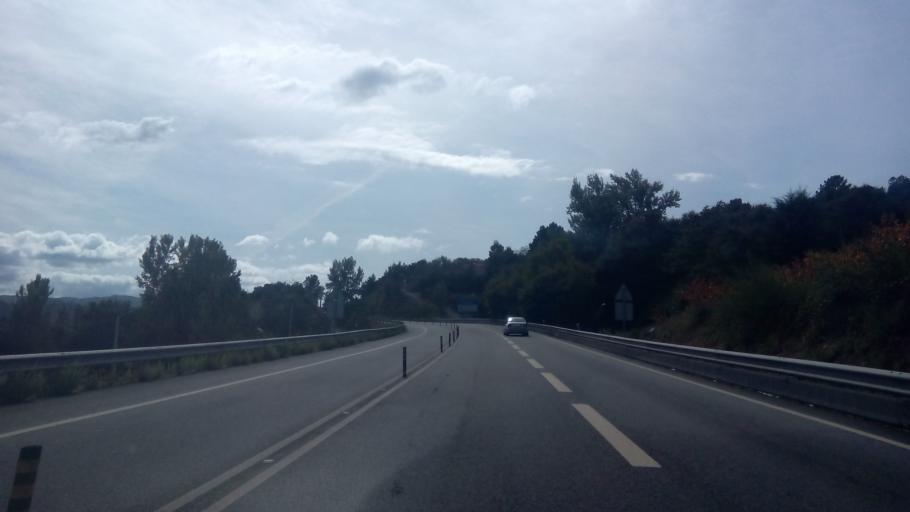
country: PT
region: Porto
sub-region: Amarante
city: Amarante
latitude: 41.2796
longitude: -7.9979
